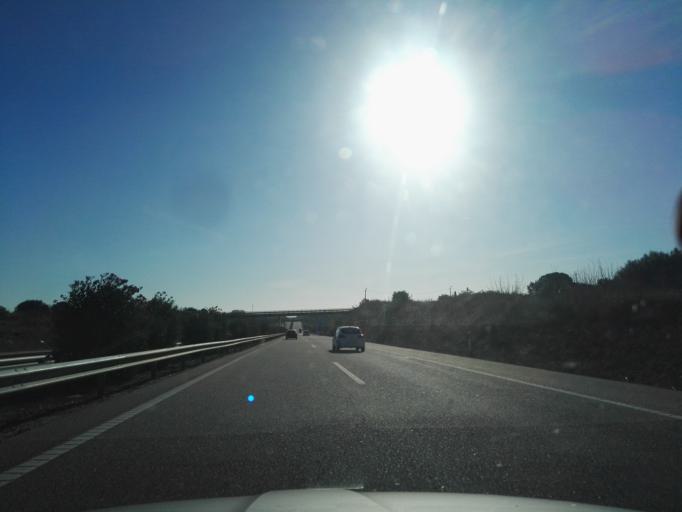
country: PT
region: Santarem
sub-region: Torres Novas
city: Torres Novas
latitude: 39.4718
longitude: -8.5768
